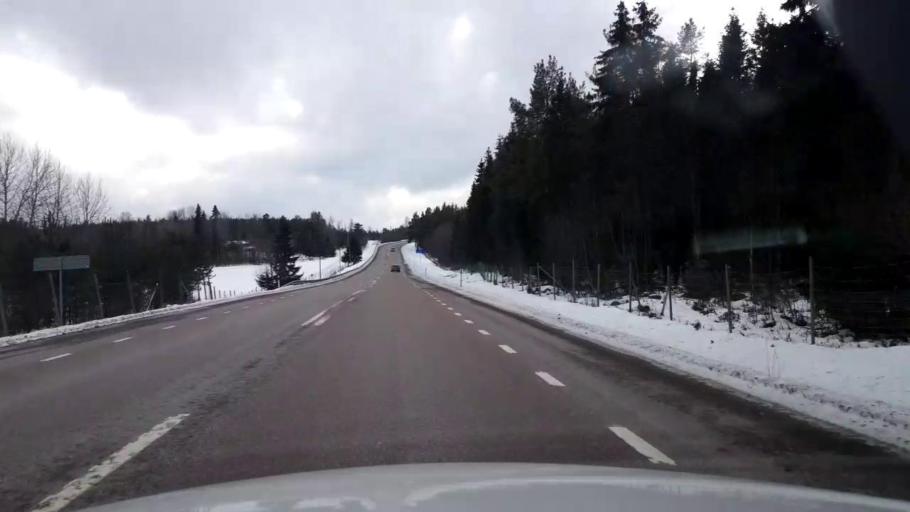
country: SE
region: Gaevleborg
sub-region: Nordanstigs Kommun
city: Bergsjoe
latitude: 61.9232
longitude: 17.2129
